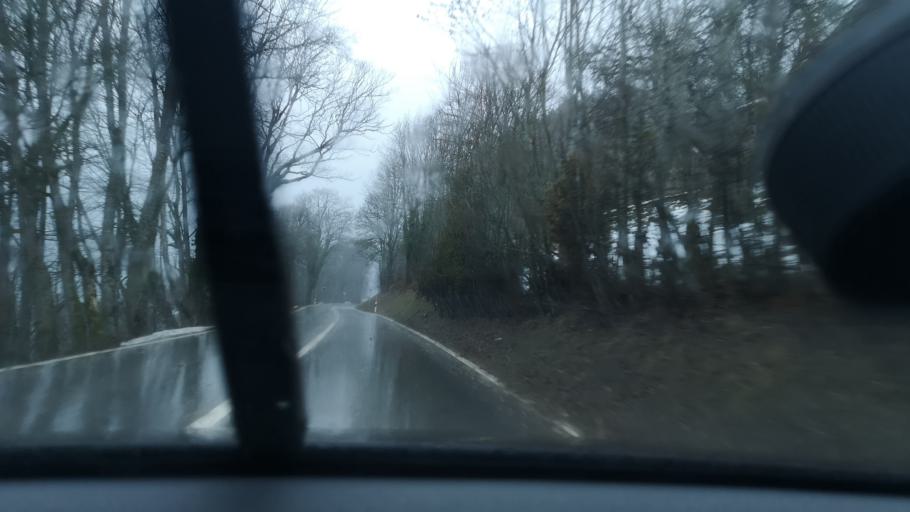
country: CH
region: Neuchatel
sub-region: Le Locle District
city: Les Ponts-de-Martel
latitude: 46.9615
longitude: 6.7664
